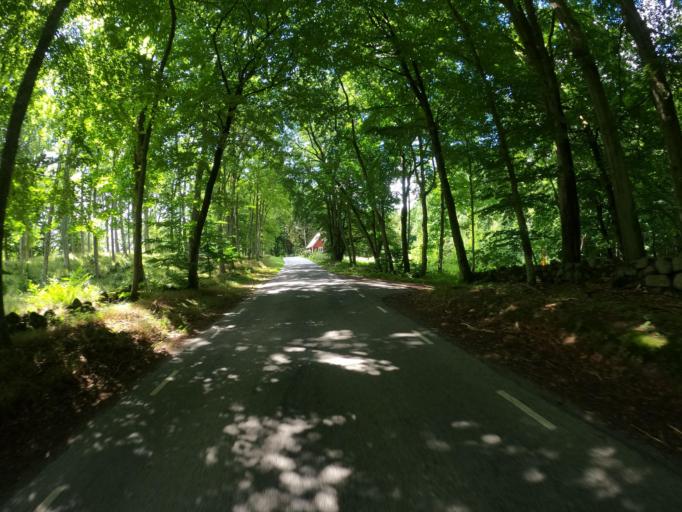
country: SE
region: Skane
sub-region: Lunds Kommun
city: Genarp
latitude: 55.5867
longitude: 13.4344
